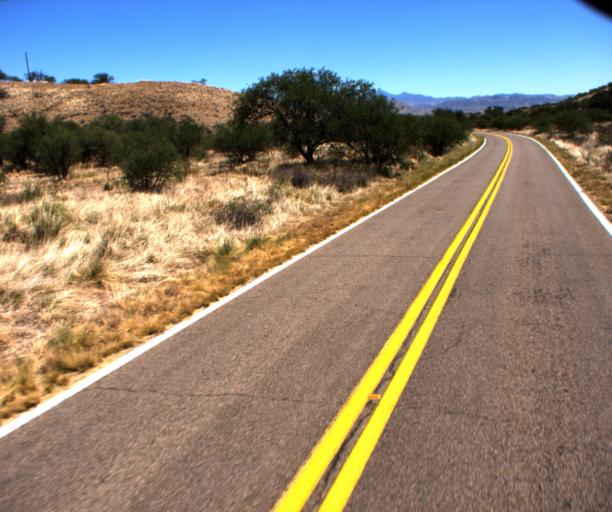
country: US
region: Arizona
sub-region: Santa Cruz County
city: Rio Rico
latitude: 31.4103
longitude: -111.0221
